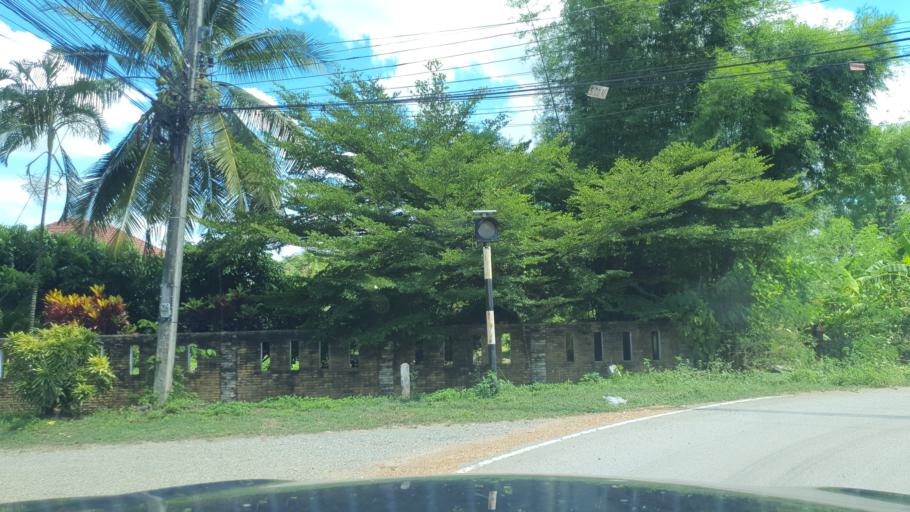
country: TH
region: Chiang Mai
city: San Sai
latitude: 18.8979
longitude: 99.0399
